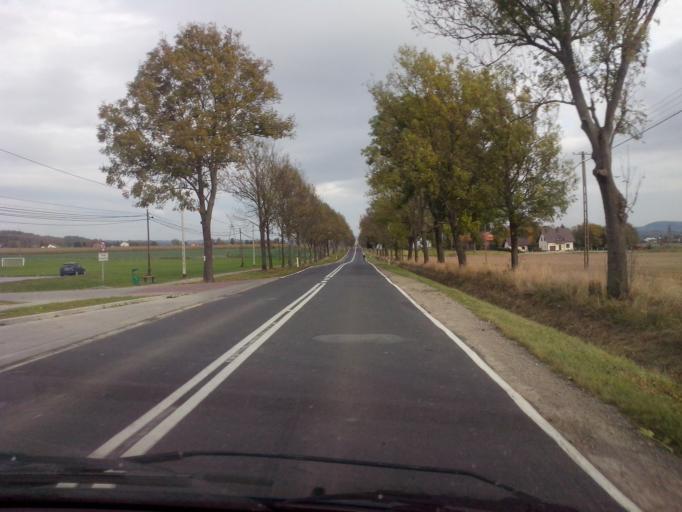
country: PL
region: Subcarpathian Voivodeship
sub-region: Powiat strzyzowski
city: Wisniowa
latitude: 49.8714
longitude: 21.6688
